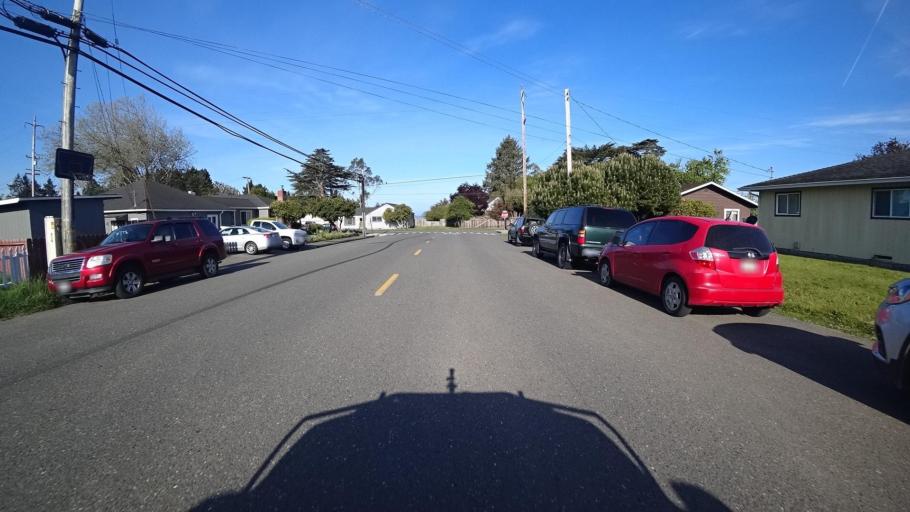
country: US
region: California
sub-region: Humboldt County
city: Bayview
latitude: 40.7637
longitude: -124.1771
